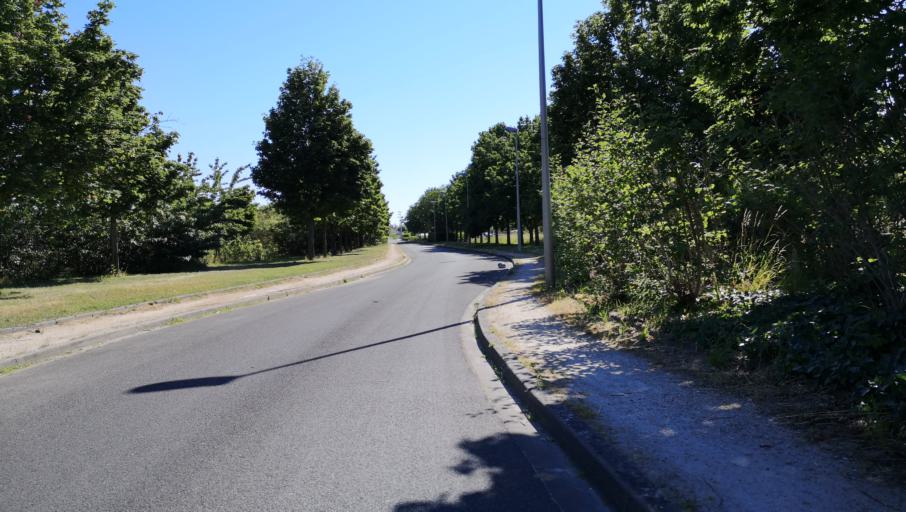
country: FR
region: Centre
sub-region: Departement du Loiret
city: Saint-Jean-de-la-Ruelle
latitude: 47.9269
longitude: 1.8798
